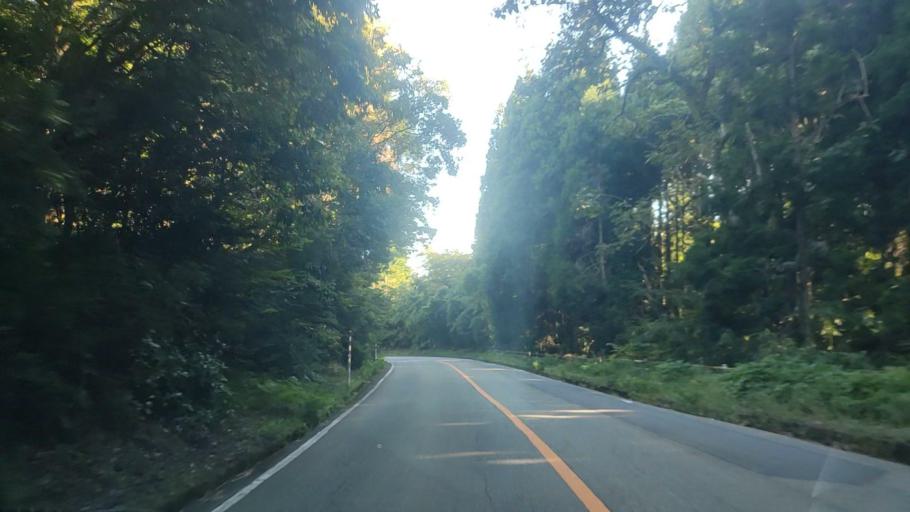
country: JP
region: Ishikawa
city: Nanao
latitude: 37.1014
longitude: 136.9486
